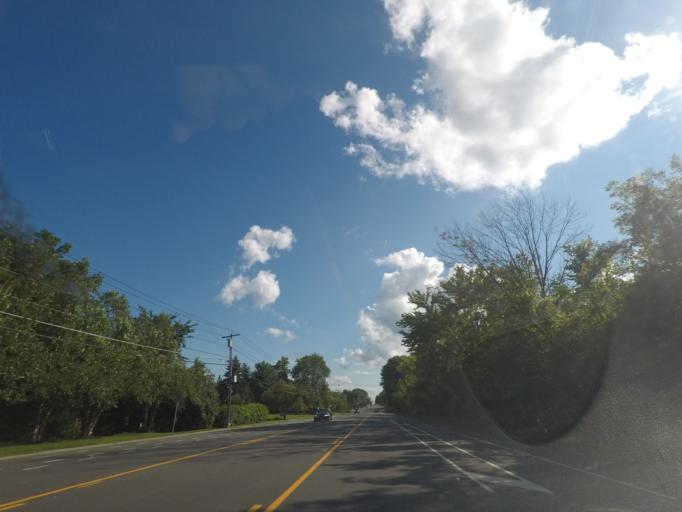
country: US
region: New York
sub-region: Albany County
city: Menands
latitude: 42.6808
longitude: -73.7428
